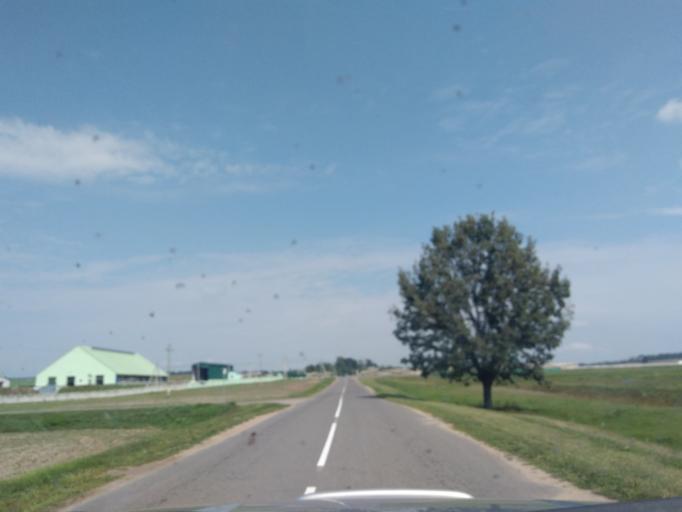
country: BY
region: Minsk
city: Valozhyn
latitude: 54.0357
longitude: 26.6047
